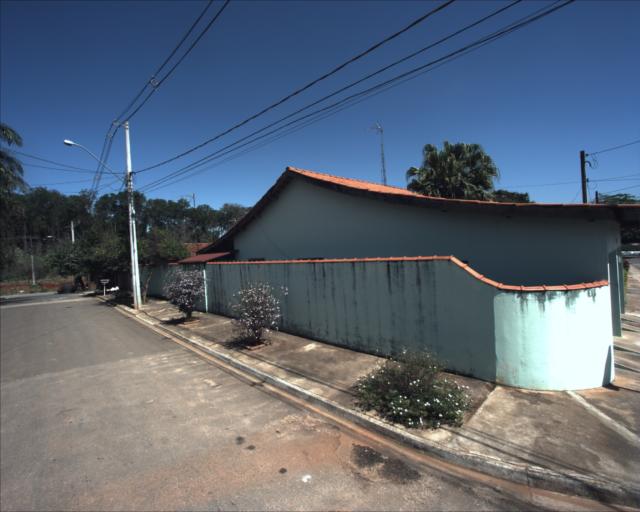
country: BR
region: Sao Paulo
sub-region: Sorocaba
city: Sorocaba
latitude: -23.4410
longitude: -47.5372
